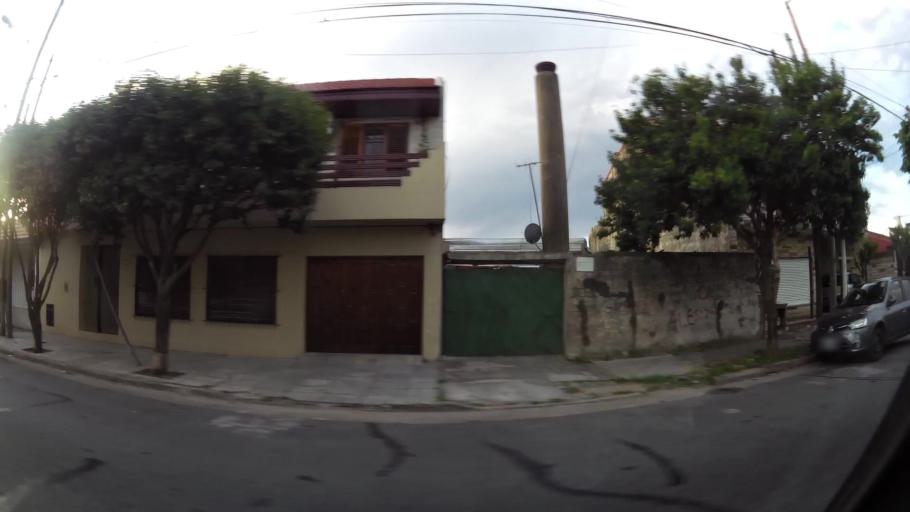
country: AR
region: Buenos Aires
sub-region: Partido de Avellaneda
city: Avellaneda
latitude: -34.7013
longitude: -58.3313
